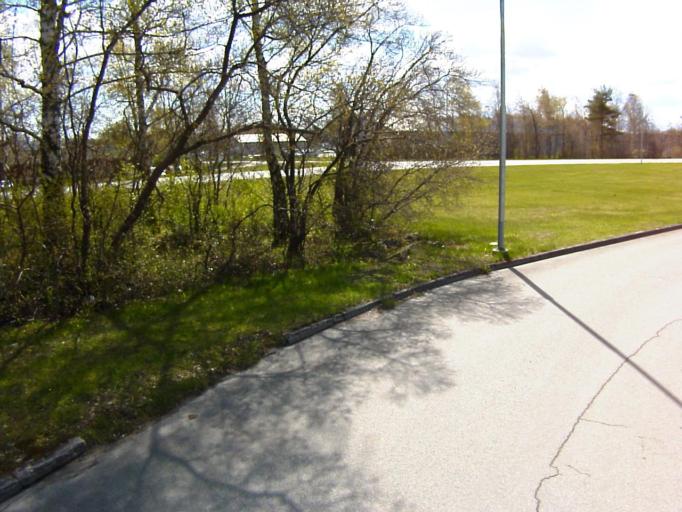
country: SE
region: Skane
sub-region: Kristianstads Kommun
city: Norra Asum
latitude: 56.0096
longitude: 14.1001
